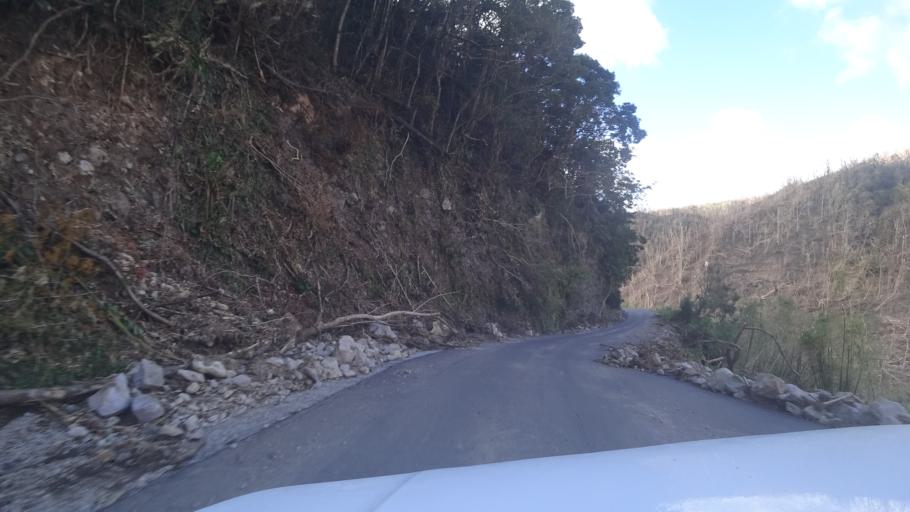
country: DM
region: Saint Luke
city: Pointe Michel
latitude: 15.2728
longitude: -61.3570
